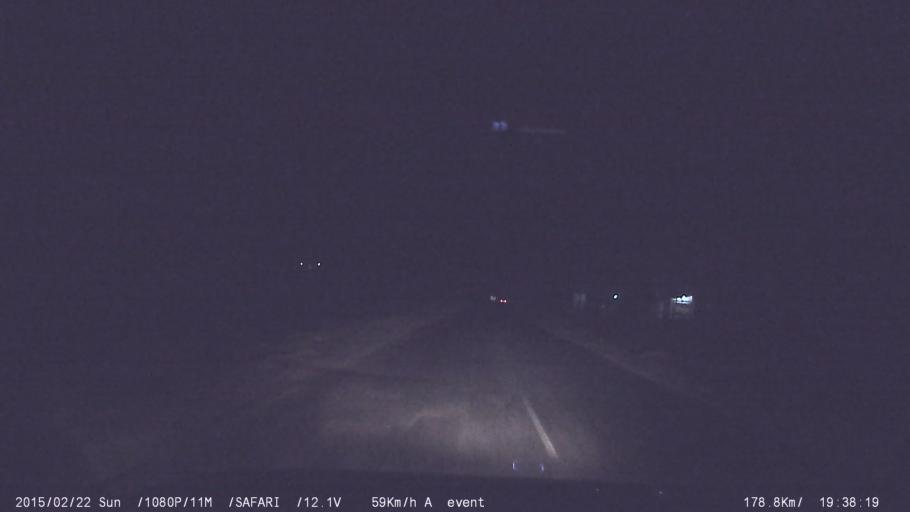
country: IN
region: Tamil Nadu
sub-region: Theni
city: Devadanappatti
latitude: 10.1425
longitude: 77.6300
